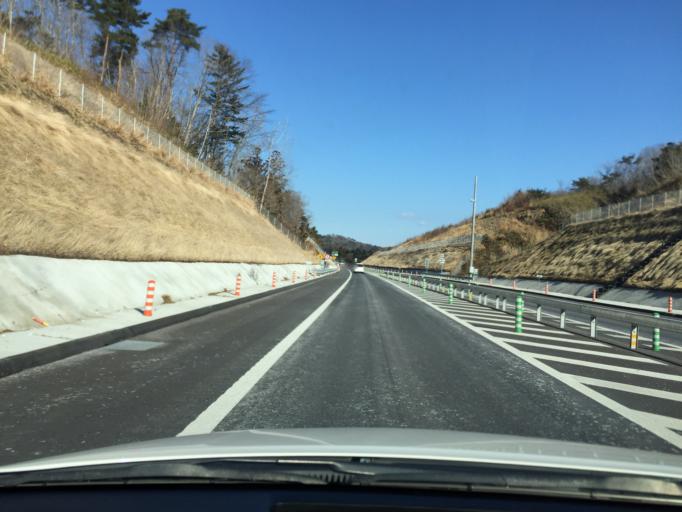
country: JP
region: Fukushima
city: Namie
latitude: 37.4190
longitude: 140.9625
